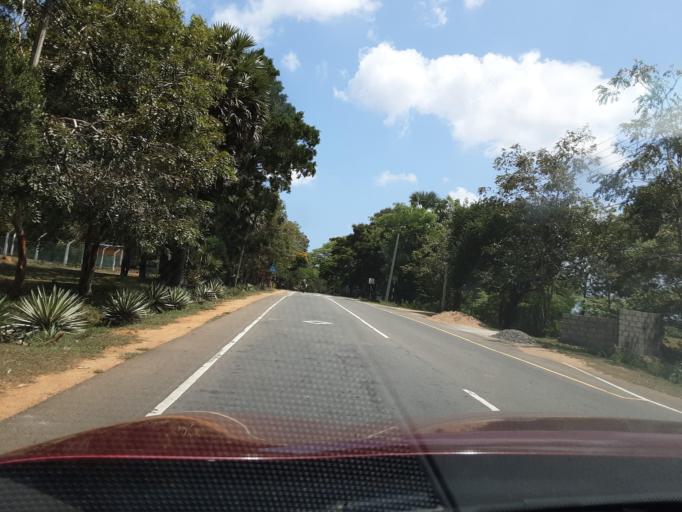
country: LK
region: Southern
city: Tangalla
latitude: 6.2496
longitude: 81.2279
